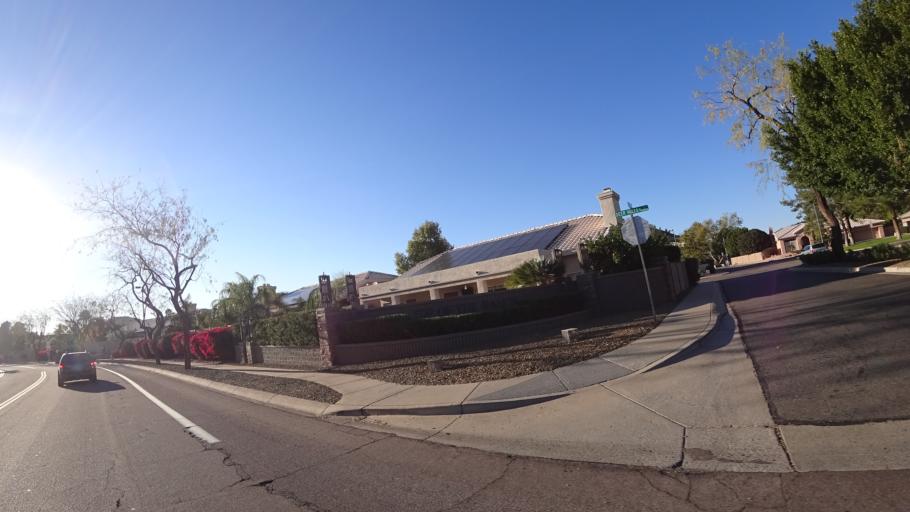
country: US
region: Arizona
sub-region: Maricopa County
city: Peoria
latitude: 33.6828
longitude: -112.1897
